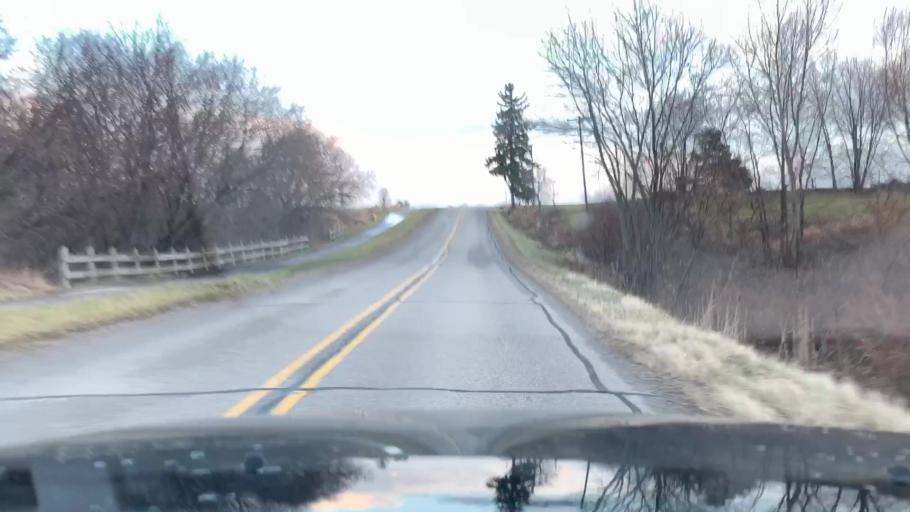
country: US
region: Michigan
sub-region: Ottawa County
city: Zeeland
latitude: 42.7762
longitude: -86.0433
